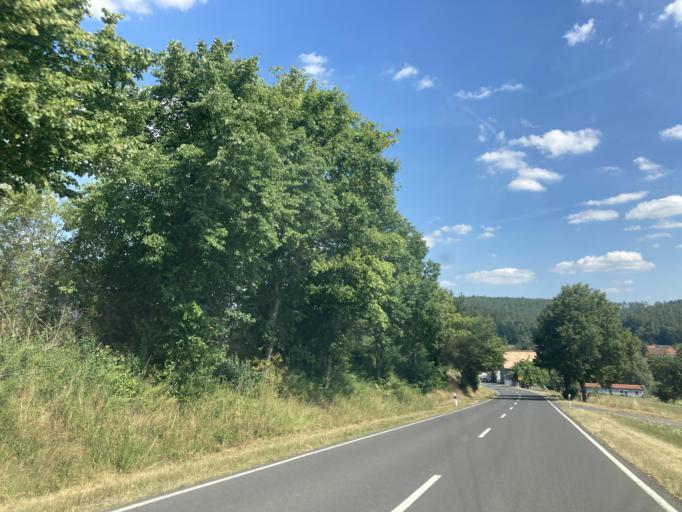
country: DE
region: Hesse
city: Grebenau
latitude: 50.7160
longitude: 9.4405
